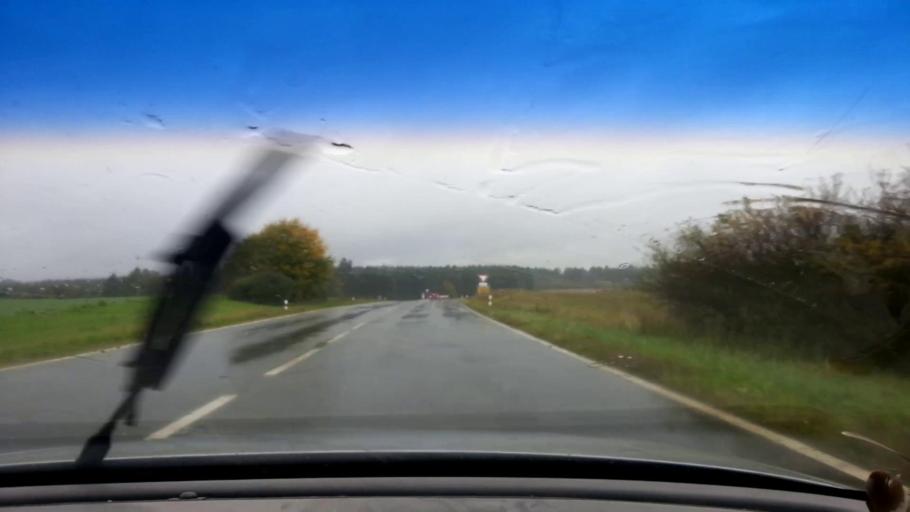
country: DE
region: Bavaria
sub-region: Upper Franconia
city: Stadelhofen
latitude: 50.0075
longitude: 11.1994
